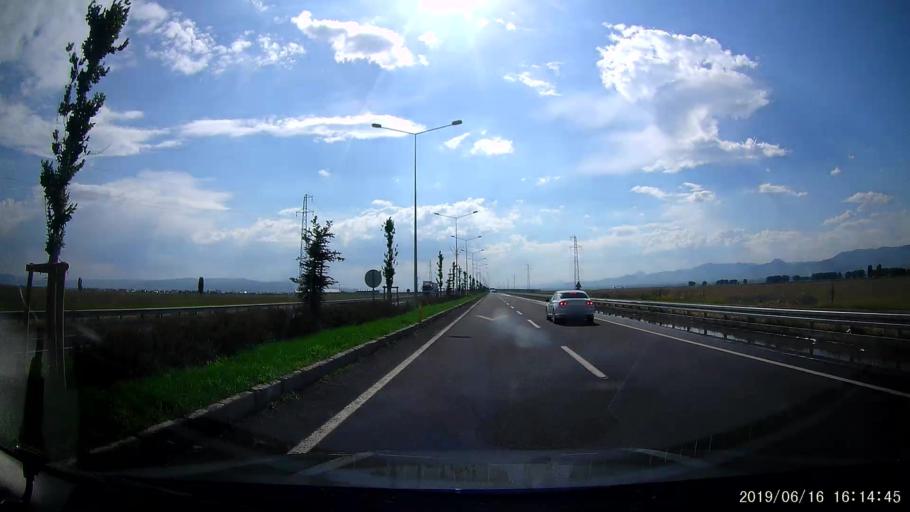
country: TR
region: Erzurum
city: Erzurum
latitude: 39.9611
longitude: 41.2410
